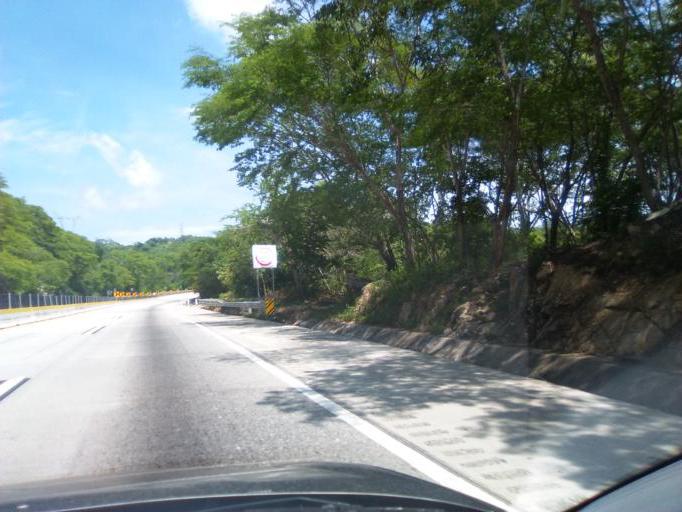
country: MX
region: Guerrero
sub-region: Acapulco de Juarez
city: Kilometro 30
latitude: 16.9475
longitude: -99.7644
